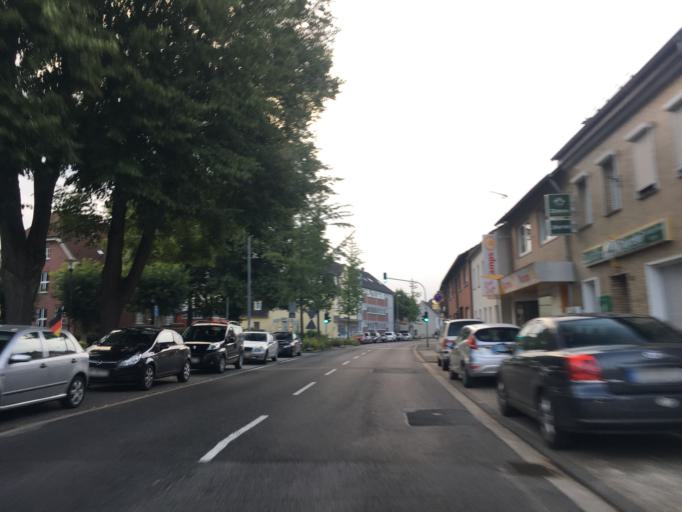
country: DE
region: North Rhine-Westphalia
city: Huckelhoven
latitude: 51.0507
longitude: 6.2273
